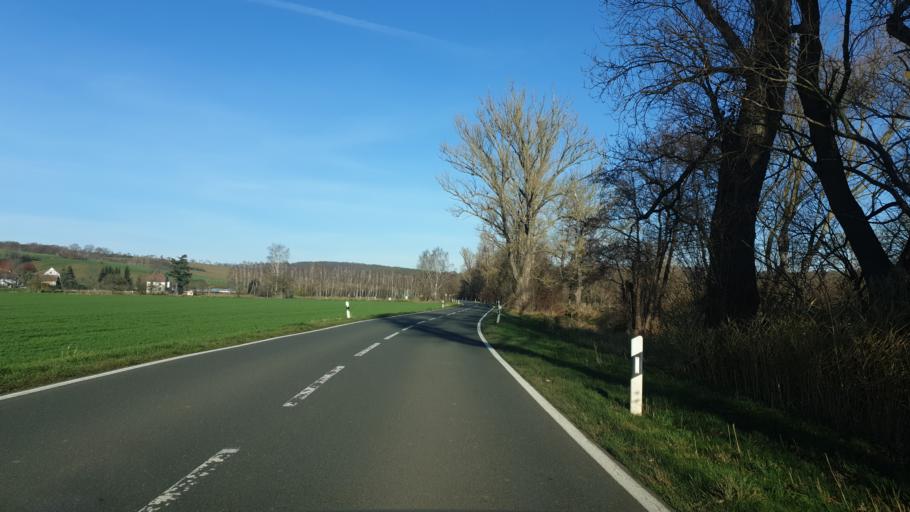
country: DE
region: Saxony-Anhalt
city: Wetterzeube
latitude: 50.9933
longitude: 11.9869
